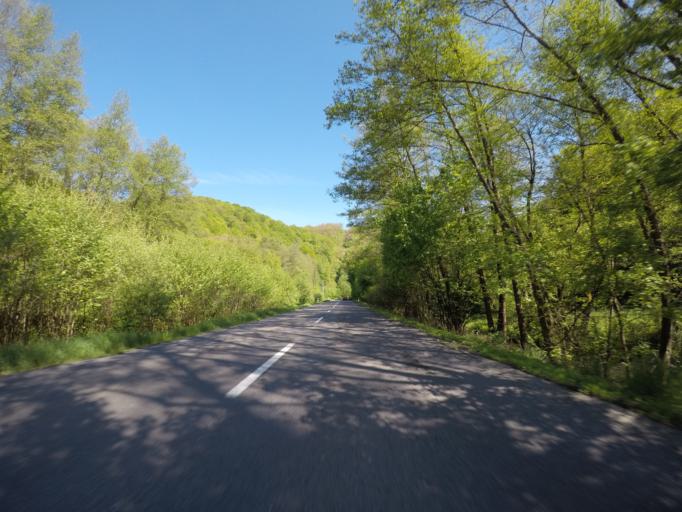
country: SK
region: Banskobystricky
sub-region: Okres Banska Bystrica
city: Banska Stiavnica
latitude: 48.5566
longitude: 19.0036
